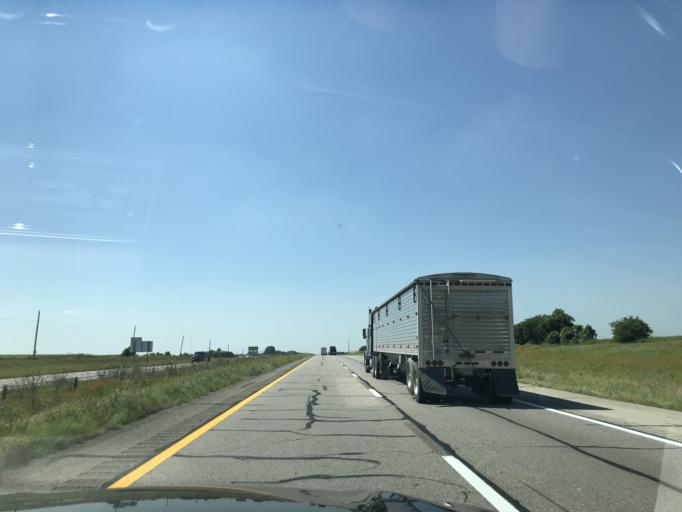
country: US
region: Texas
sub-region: Johnson County
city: Alvarado
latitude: 32.3505
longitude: -97.1957
